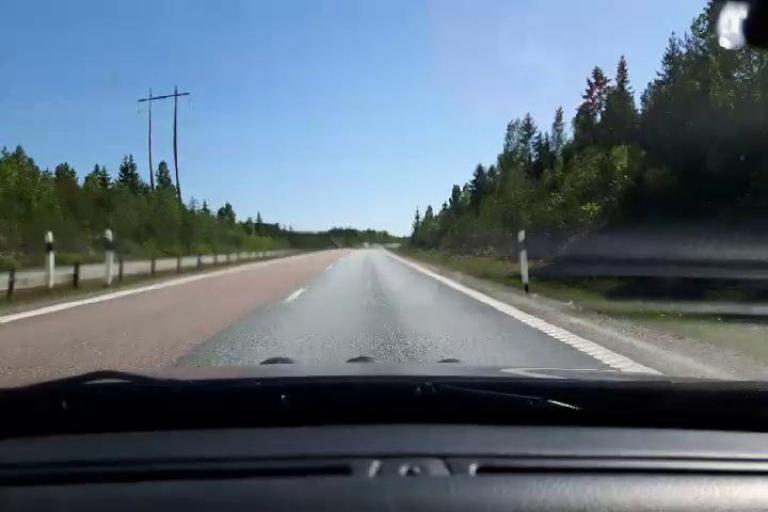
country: SE
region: Gaevleborg
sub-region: Hudiksvalls Kommun
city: Iggesund
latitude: 61.5061
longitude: 16.9861
